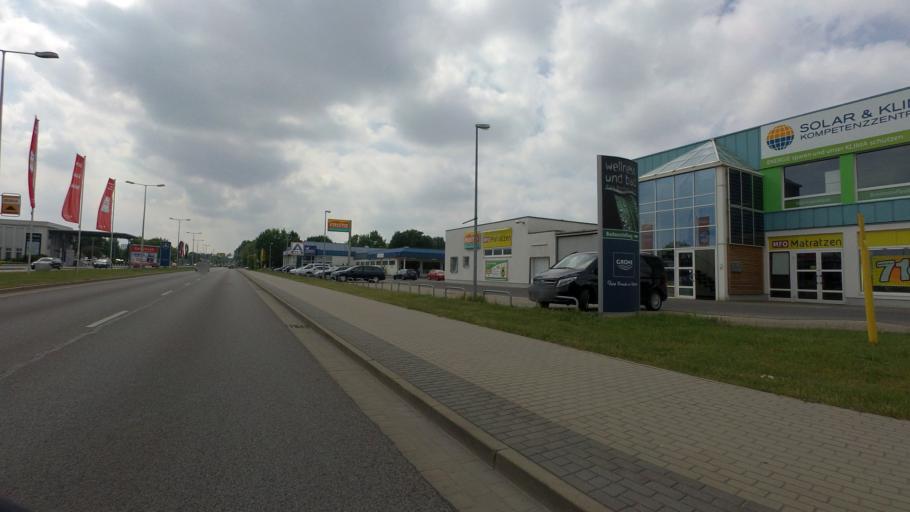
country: DE
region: Brandenburg
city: Cottbus
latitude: 51.7663
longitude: 14.3582
